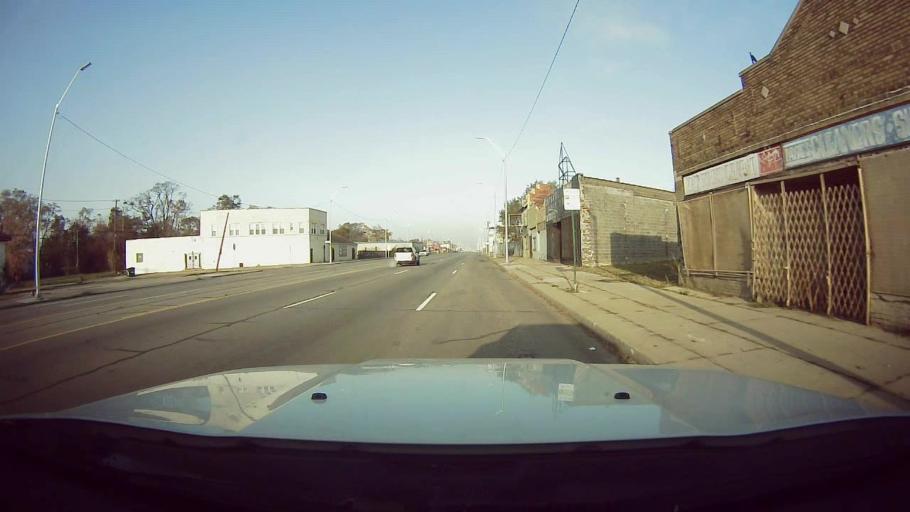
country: US
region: Michigan
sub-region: Wayne County
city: Dearborn
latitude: 42.3756
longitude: -83.1559
